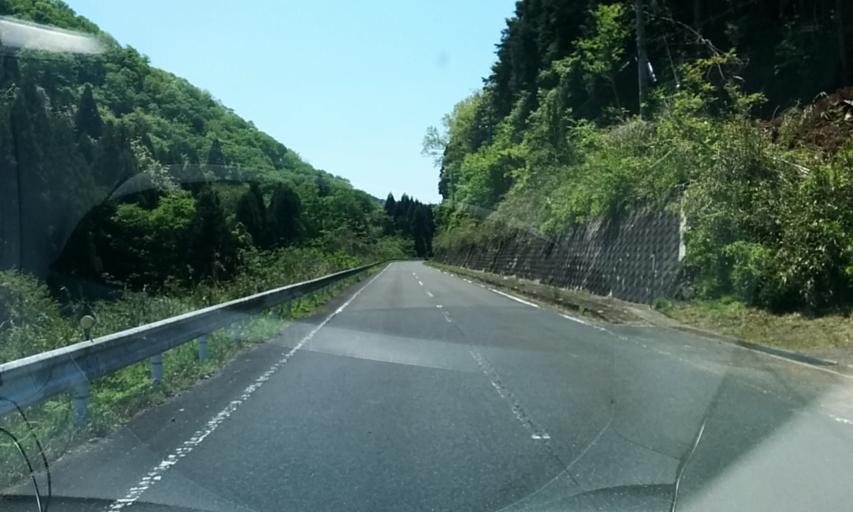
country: JP
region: Kyoto
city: Ayabe
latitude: 35.2153
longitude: 135.2941
